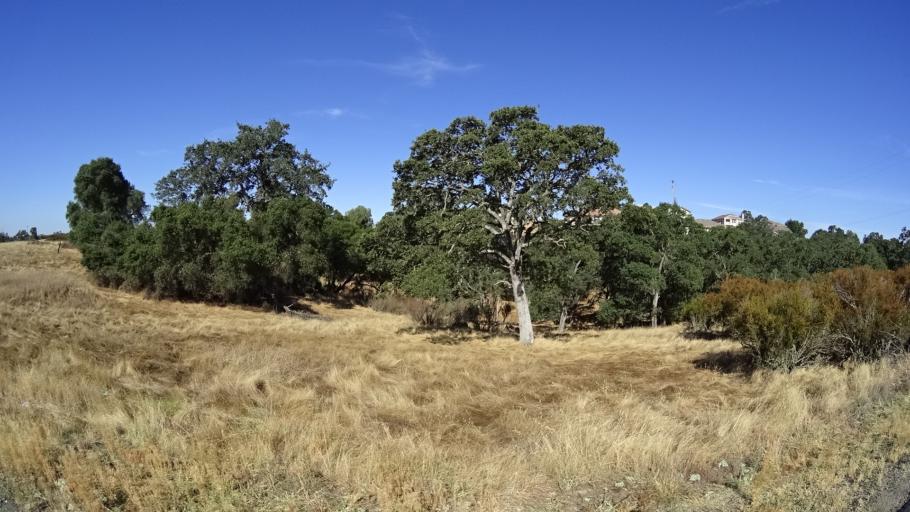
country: US
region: California
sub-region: Calaveras County
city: Valley Springs
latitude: 38.1602
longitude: -120.8151
